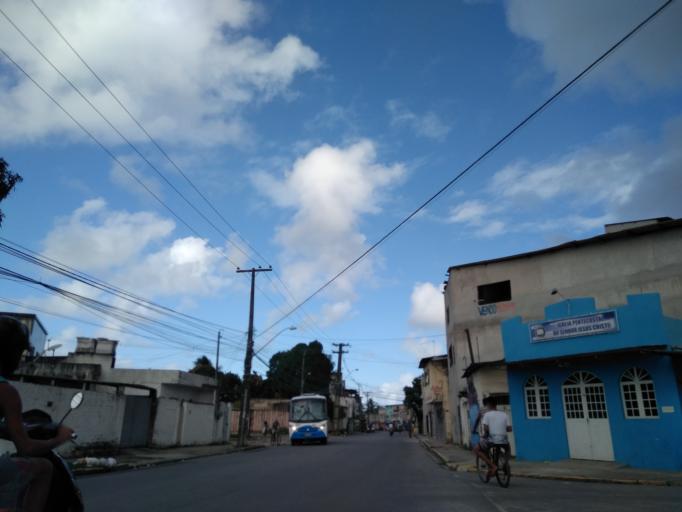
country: BR
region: Pernambuco
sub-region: Recife
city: Recife
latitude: -8.0731
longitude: -34.9239
